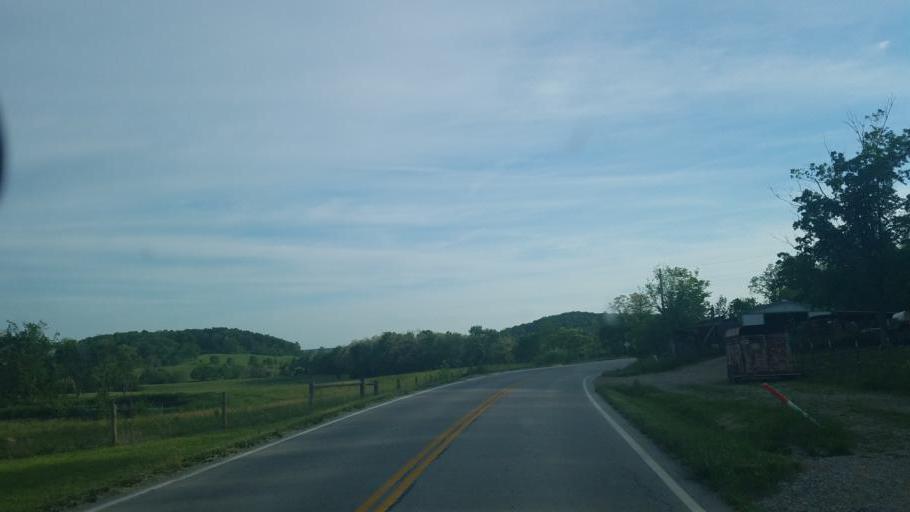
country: US
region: Ohio
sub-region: Ross County
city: Frankfort
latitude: 39.4174
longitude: -83.2703
